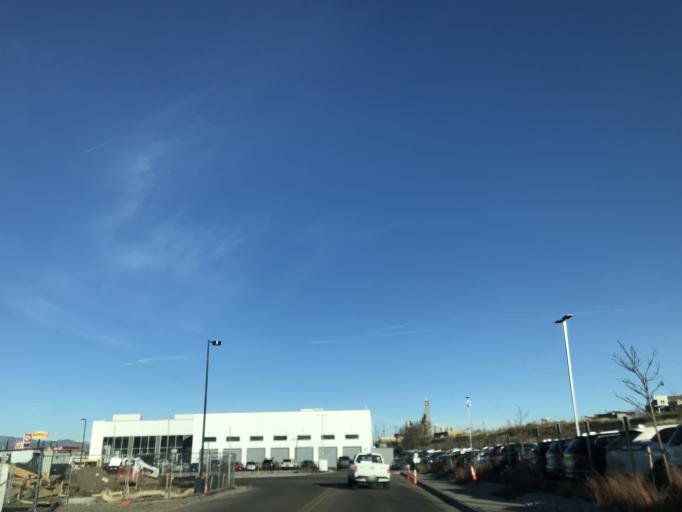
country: US
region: Colorado
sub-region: Denver County
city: Denver
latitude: 39.7089
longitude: -104.9951
